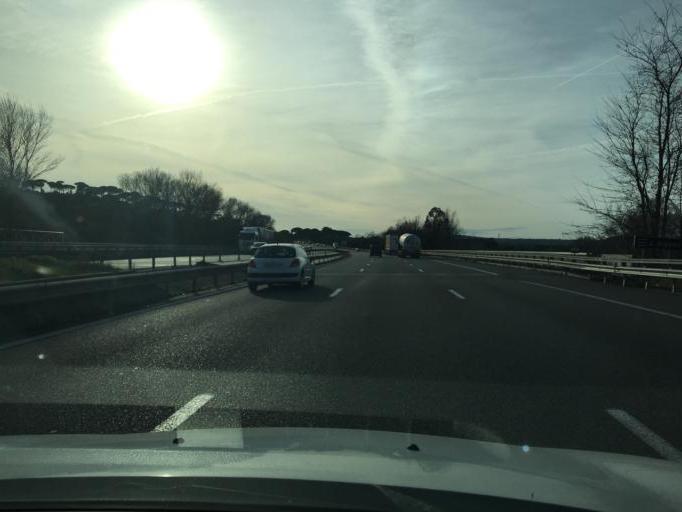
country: FR
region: Provence-Alpes-Cote d'Azur
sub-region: Departement du Var
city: Le Muy
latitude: 43.4646
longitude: 6.5704
